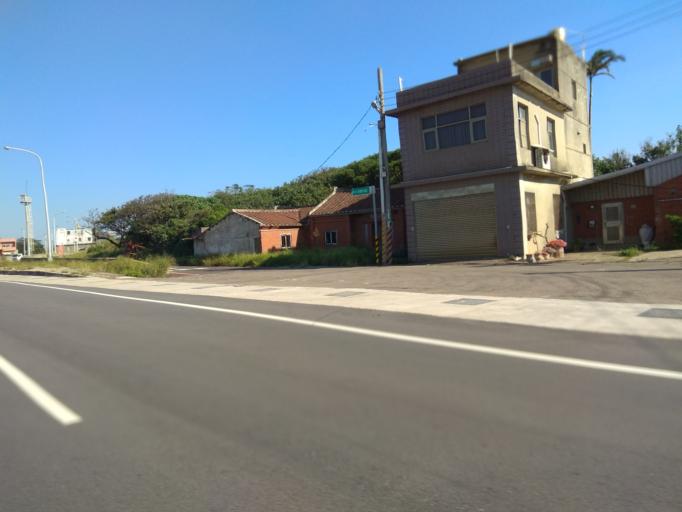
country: TW
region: Taiwan
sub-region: Hsinchu
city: Zhubei
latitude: 25.0245
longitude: 121.0612
